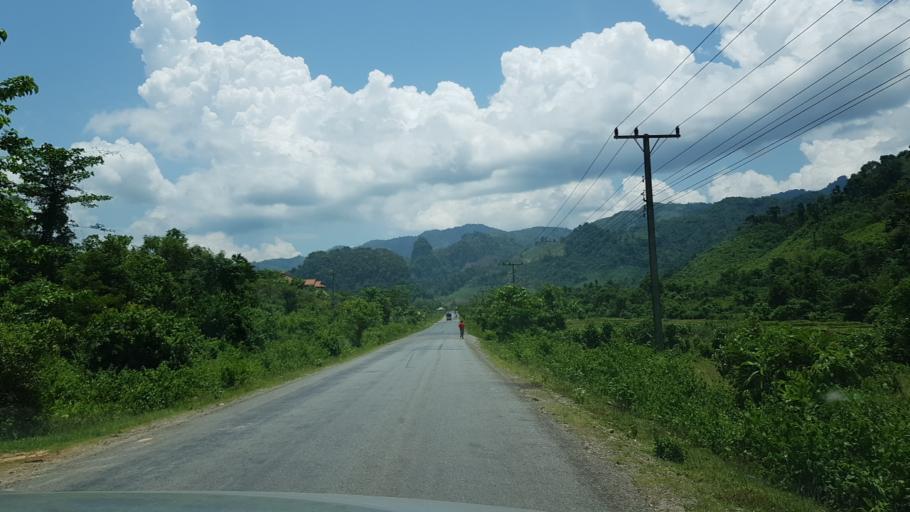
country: LA
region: Vientiane
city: Muang Kasi
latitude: 19.1273
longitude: 102.2411
